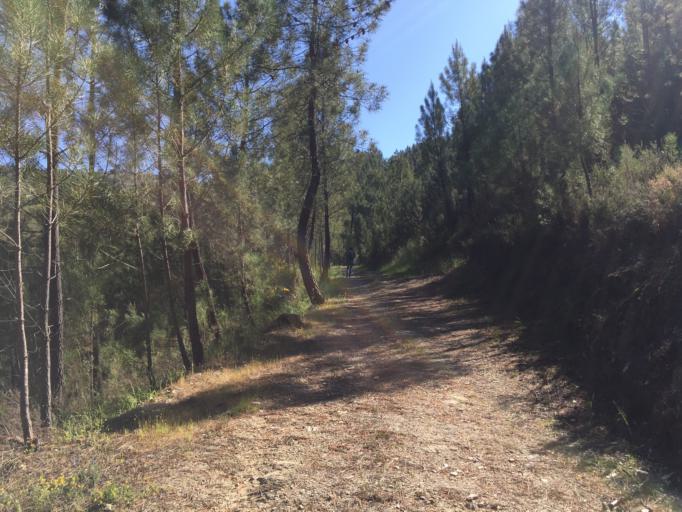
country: PT
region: Coimbra
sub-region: Pampilhosa da Serra
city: Pampilhosa da Serra
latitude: 40.0858
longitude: -7.7834
